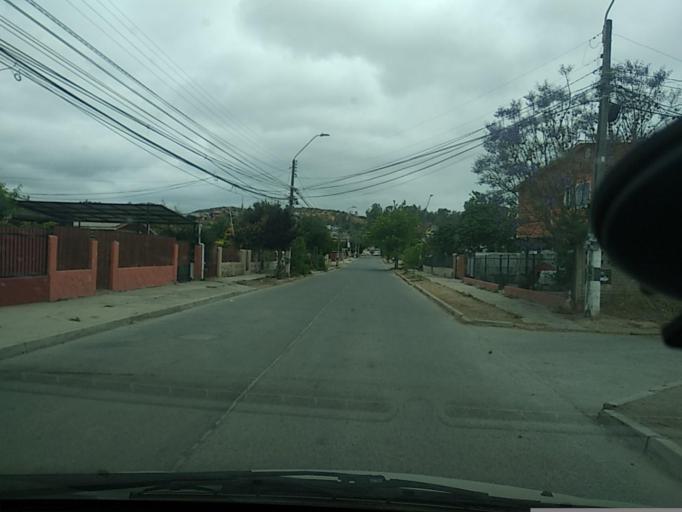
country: CL
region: Valparaiso
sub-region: Provincia de Marga Marga
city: Villa Alemana
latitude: -33.0399
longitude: -71.3618
